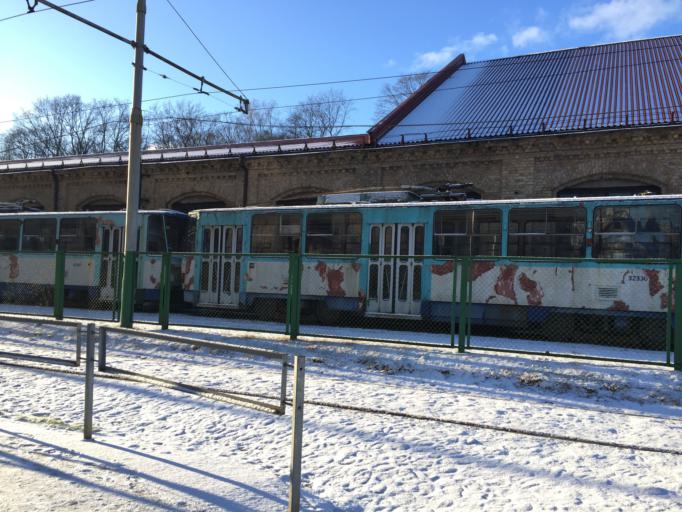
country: LV
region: Riga
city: Riga
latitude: 56.9206
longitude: 24.0918
